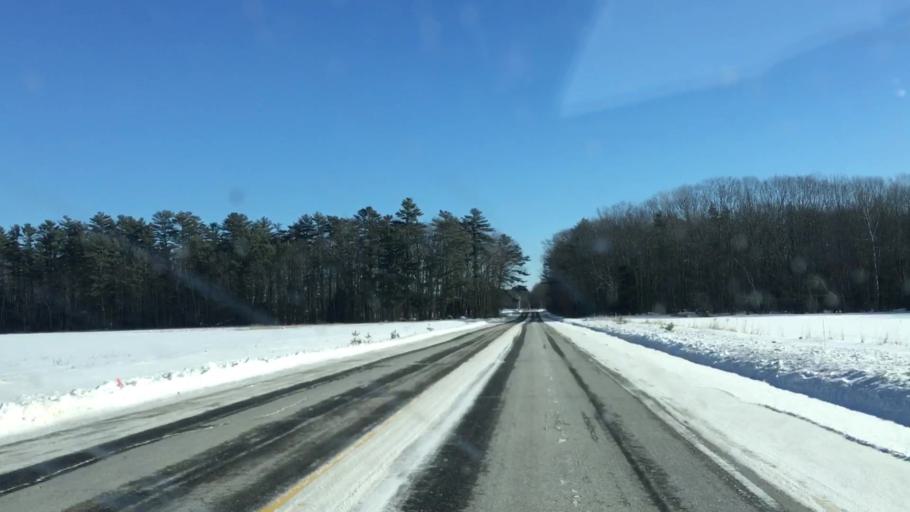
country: US
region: Maine
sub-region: Cumberland County
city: Brunswick
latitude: 43.8920
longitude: -69.9904
